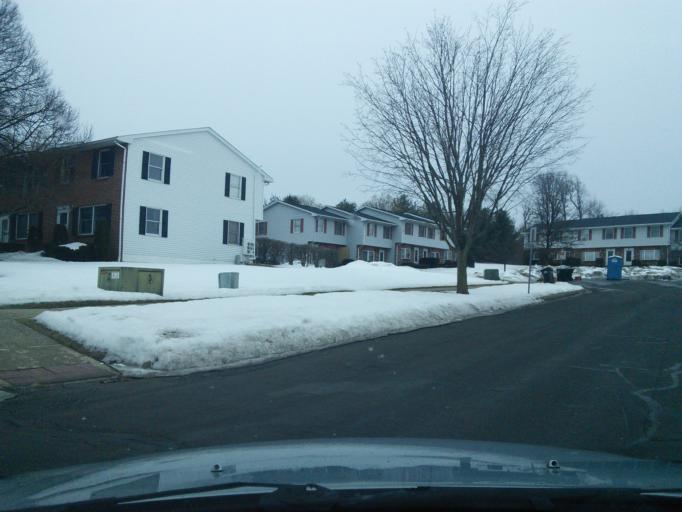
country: US
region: Pennsylvania
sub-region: Centre County
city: State College
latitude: 40.7718
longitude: -77.8649
